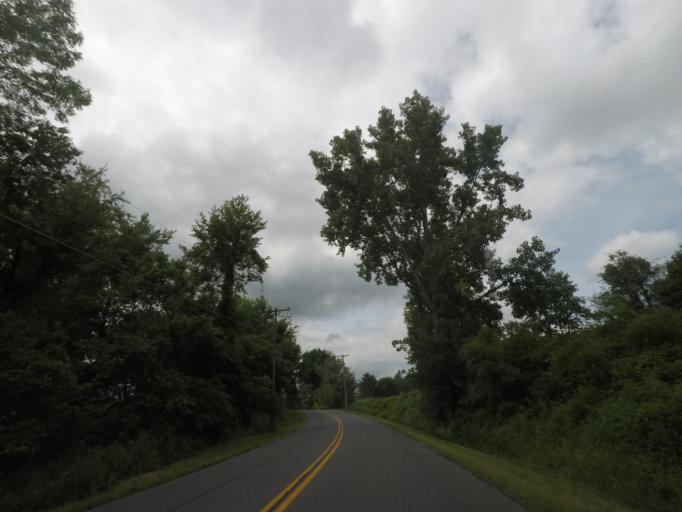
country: US
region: New York
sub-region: Saratoga County
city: Stillwater
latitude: 43.0005
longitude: -73.6945
